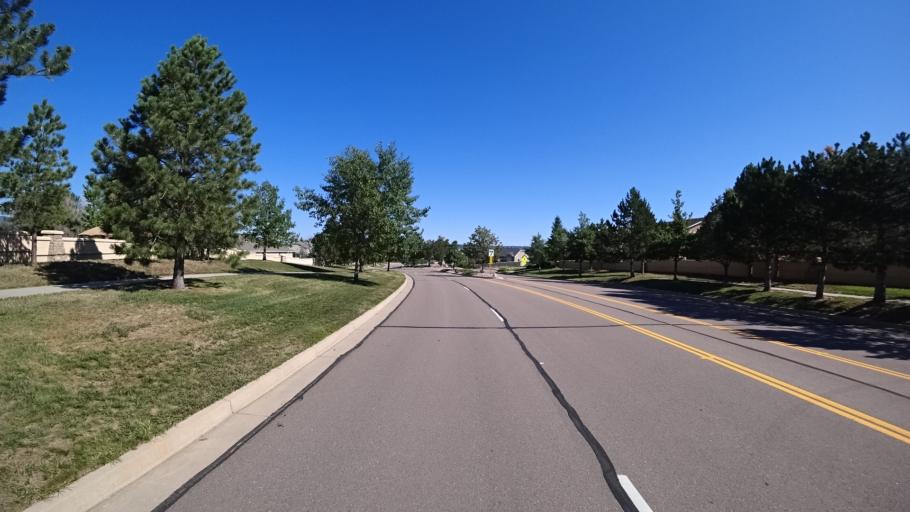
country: US
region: Colorado
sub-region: El Paso County
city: Black Forest
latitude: 38.9799
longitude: -104.7703
